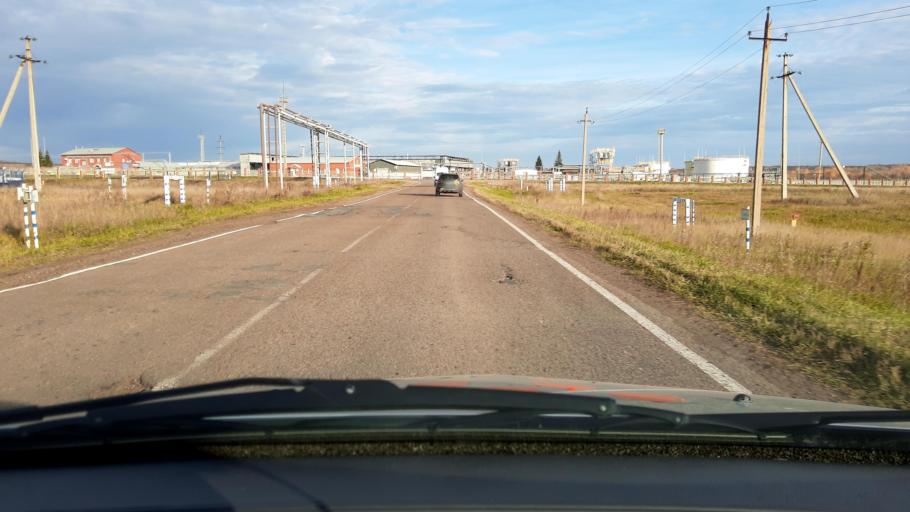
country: RU
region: Bashkortostan
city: Mikhaylovka
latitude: 54.8227
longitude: 55.7653
